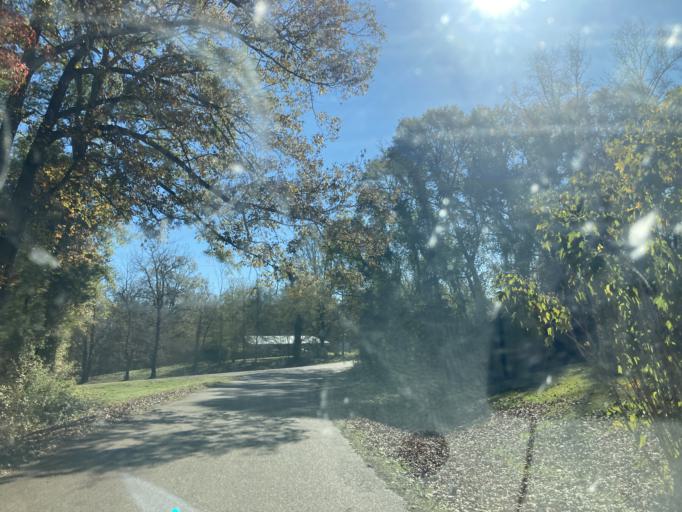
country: US
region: Mississippi
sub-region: Hinds County
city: Lynchburg
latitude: 32.5891
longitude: -90.5213
